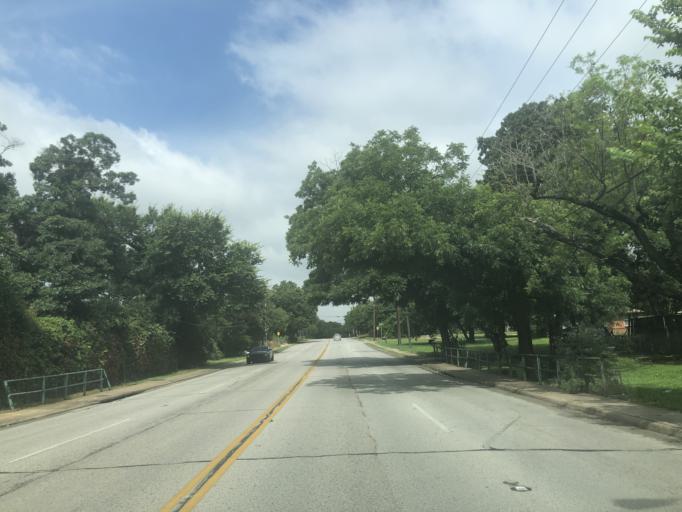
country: US
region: Texas
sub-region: Dallas County
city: Irving
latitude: 32.8019
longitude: -96.9649
